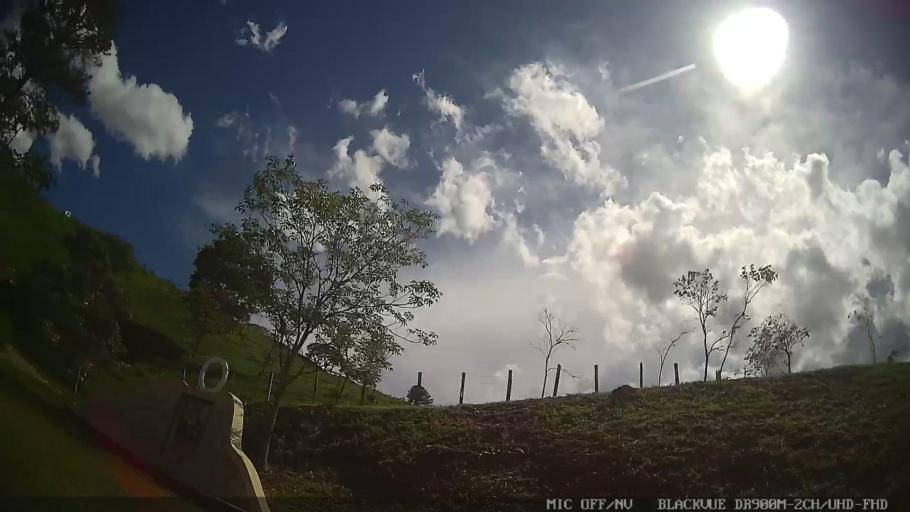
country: BR
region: Sao Paulo
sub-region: Pedreira
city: Pedreira
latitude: -22.7437
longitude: -46.9073
